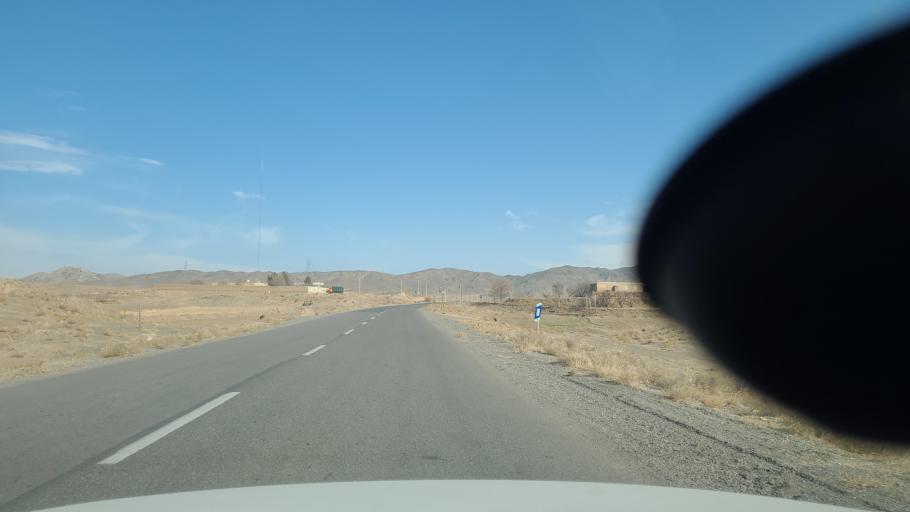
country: IR
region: Razavi Khorasan
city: Fariman
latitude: 35.5957
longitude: 59.6947
